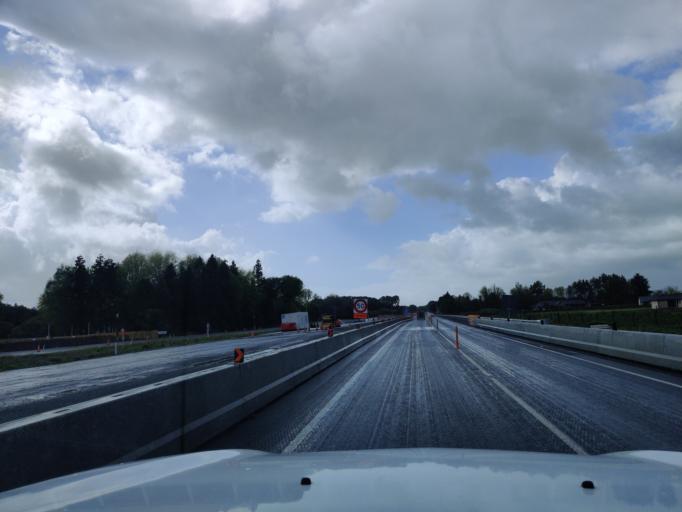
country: NZ
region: Waikato
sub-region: Hamilton City
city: Hamilton
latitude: -37.8207
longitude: 175.3473
